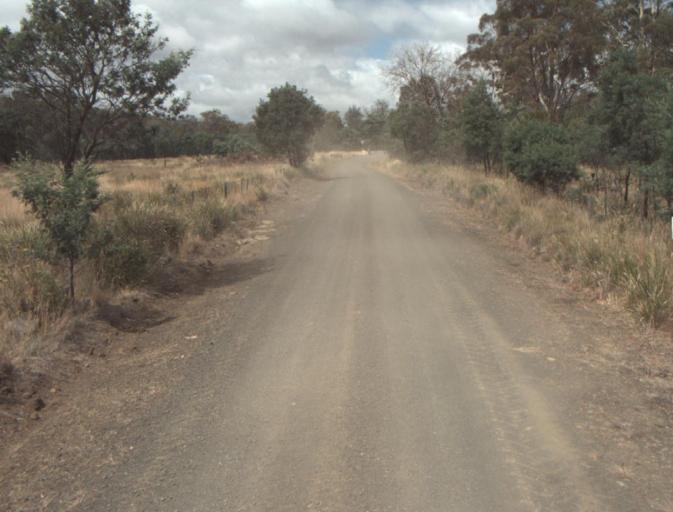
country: AU
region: Tasmania
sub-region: Northern Midlands
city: Evandale
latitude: -41.5053
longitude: 147.3577
